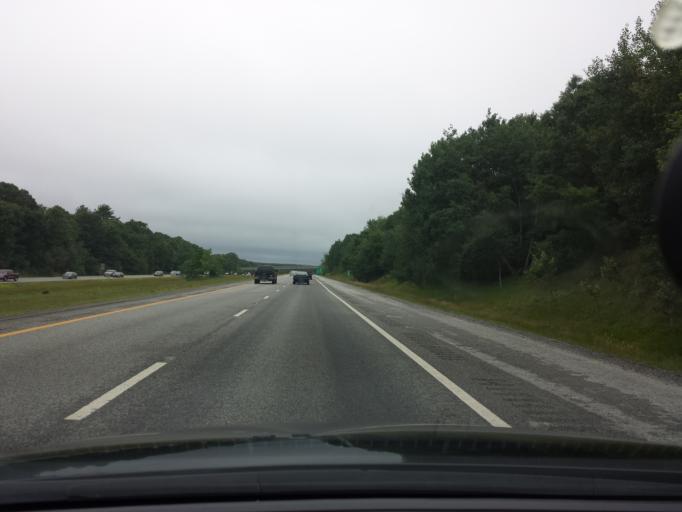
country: US
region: Rhode Island
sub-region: Kent County
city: West Greenwich
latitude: 41.5866
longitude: -71.6593
